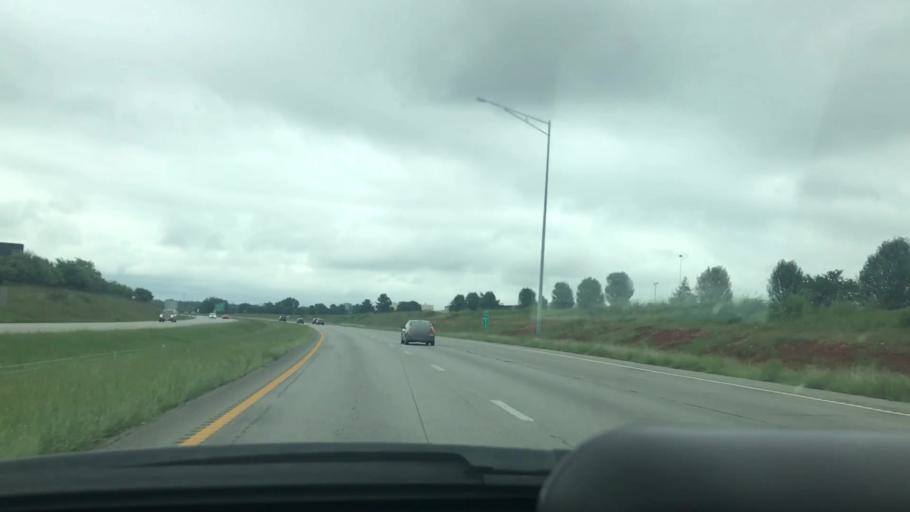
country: US
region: Missouri
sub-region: Jasper County
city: Duquesne
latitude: 37.0467
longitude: -94.4726
